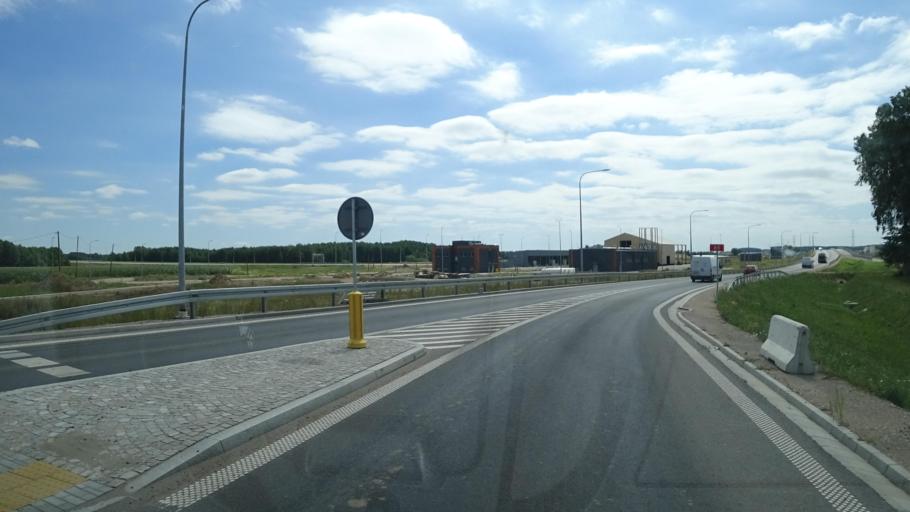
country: PL
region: Warmian-Masurian Voivodeship
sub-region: Powiat elcki
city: Elk
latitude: 53.7587
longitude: 22.3388
